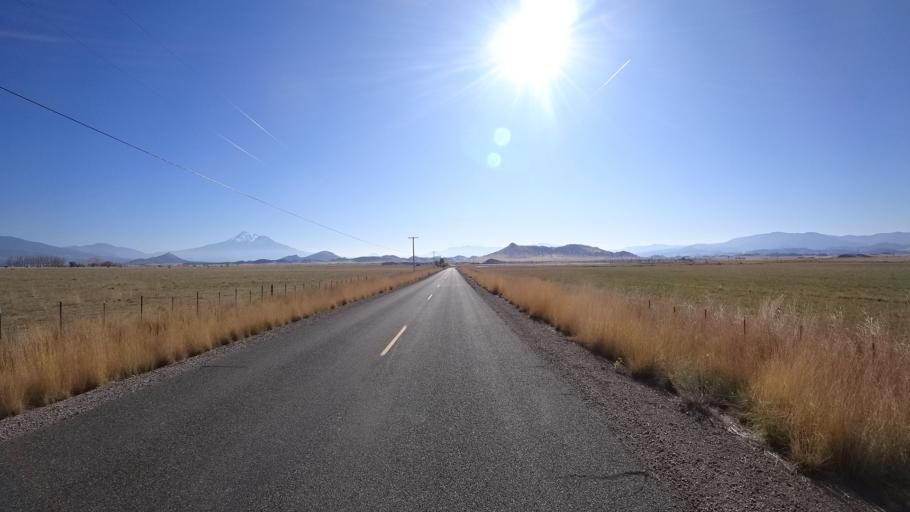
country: US
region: California
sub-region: Siskiyou County
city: Montague
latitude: 41.7302
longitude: -122.4574
